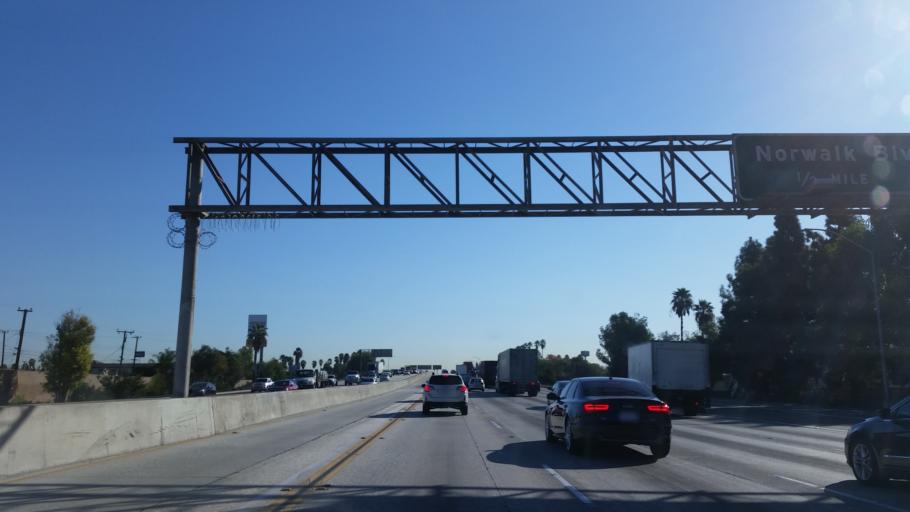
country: US
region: California
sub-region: Los Angeles County
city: Artesia
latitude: 33.8764
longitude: -118.0870
